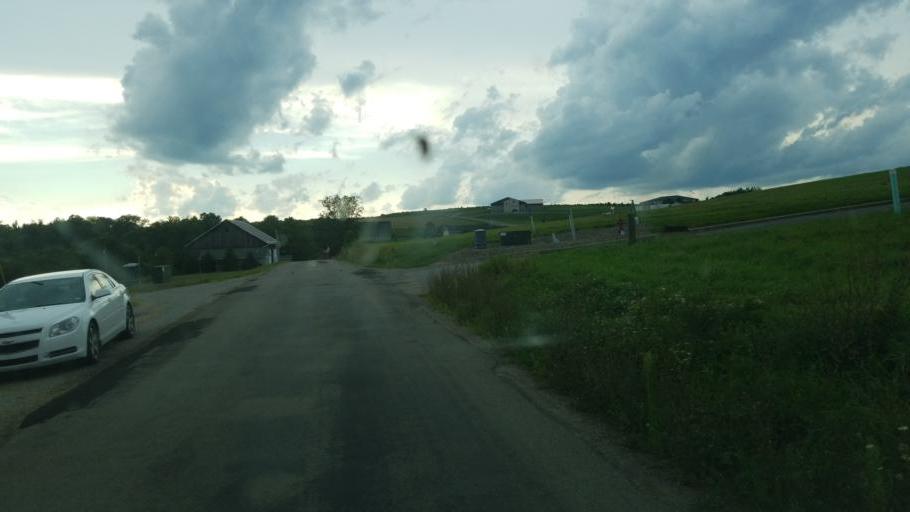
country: US
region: Pennsylvania
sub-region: Clarion County
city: Clarion
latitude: 41.1785
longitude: -79.3917
